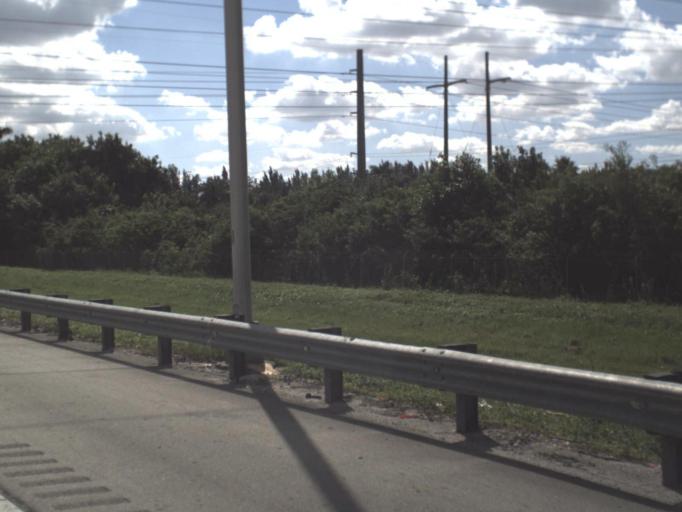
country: US
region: Florida
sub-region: Broward County
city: Davie
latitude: 26.0563
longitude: -80.2152
